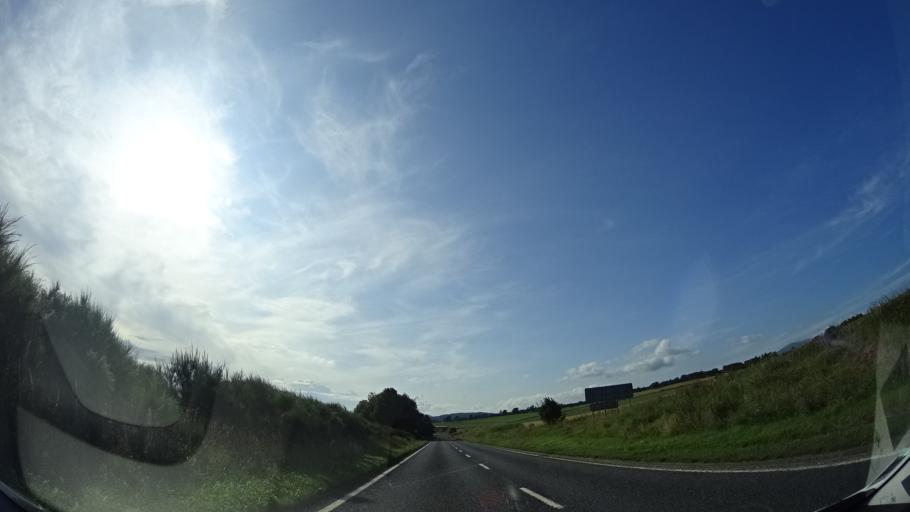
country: GB
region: Scotland
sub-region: Highland
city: Muir of Ord
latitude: 57.5590
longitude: -4.5470
